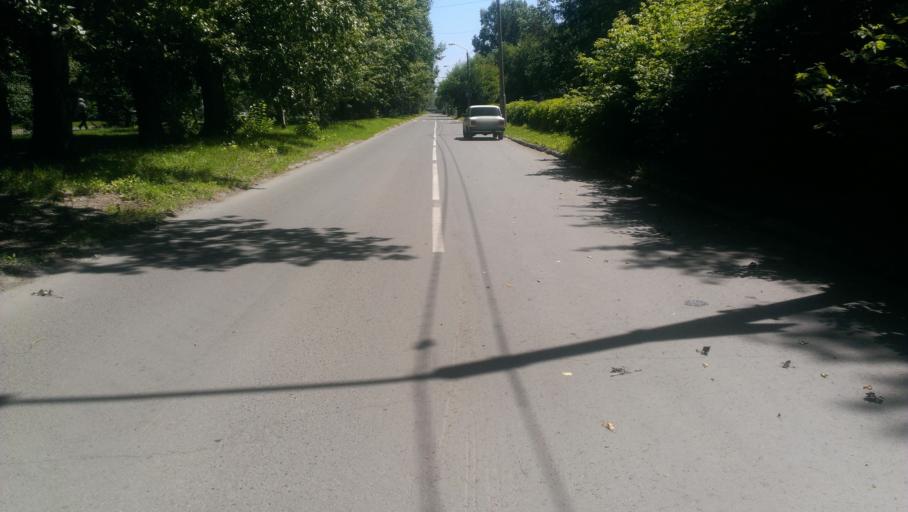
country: RU
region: Altai Krai
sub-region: Gorod Barnaulskiy
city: Barnaul
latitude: 53.3574
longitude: 83.7260
